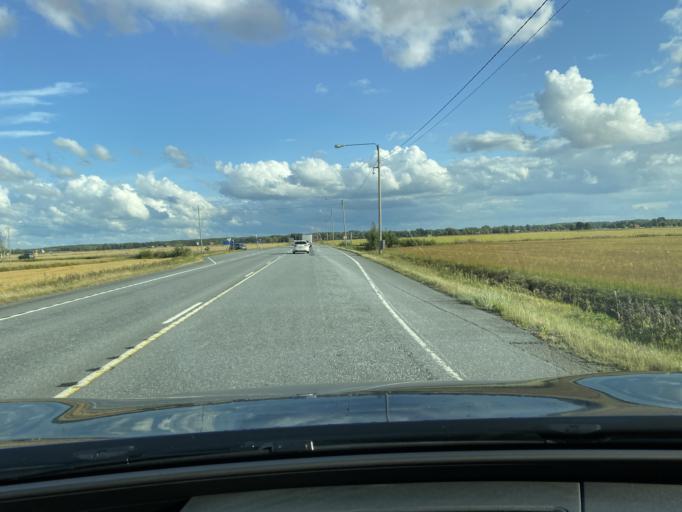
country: FI
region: Southern Ostrobothnia
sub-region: Seinaejoki
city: Kauhava
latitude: 63.1064
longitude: 22.9596
